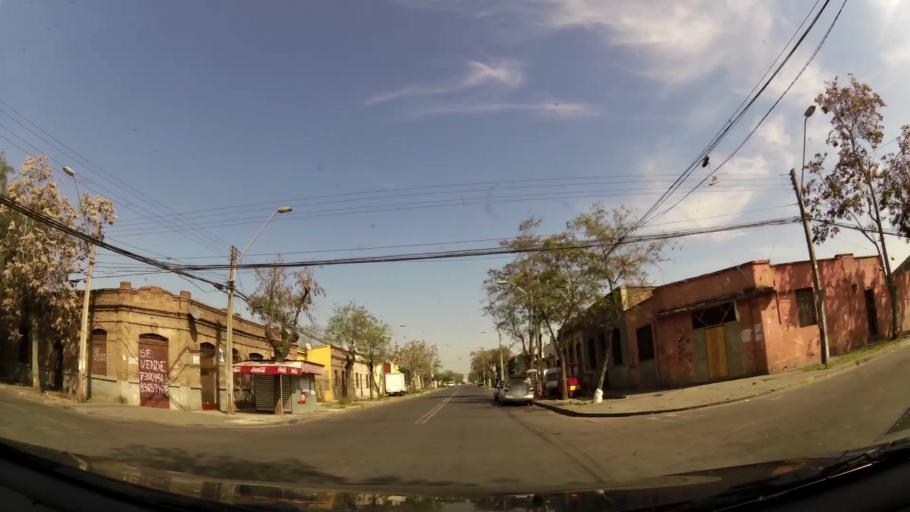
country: CL
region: Santiago Metropolitan
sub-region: Provincia de Santiago
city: Santiago
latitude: -33.4063
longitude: -70.6352
